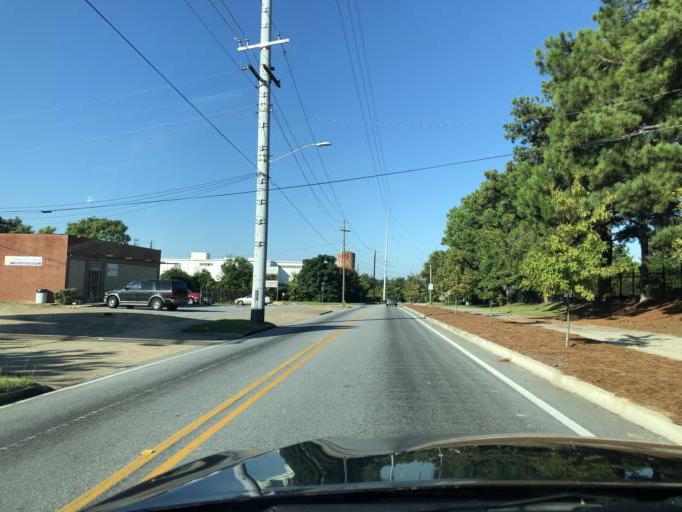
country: US
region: Georgia
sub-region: Muscogee County
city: Columbus
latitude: 32.4763
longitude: -84.9826
